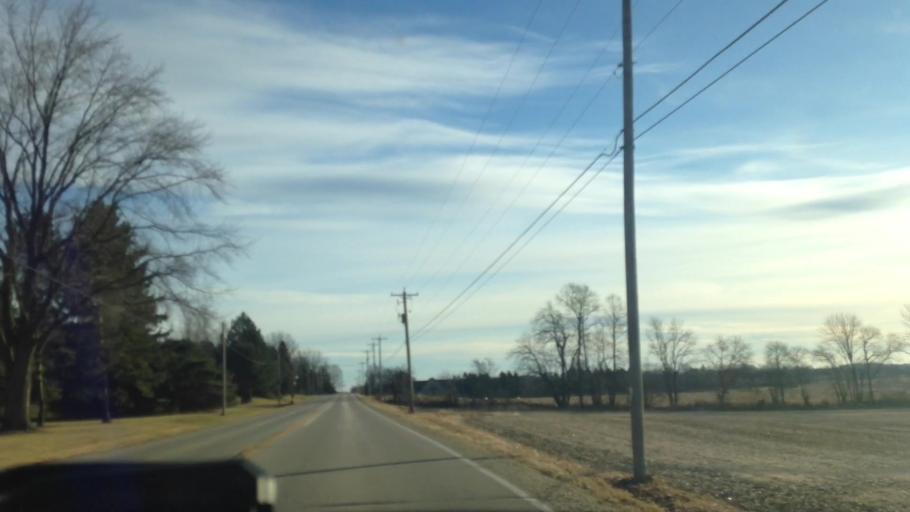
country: US
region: Wisconsin
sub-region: Washington County
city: Jackson
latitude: 43.2945
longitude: -88.1296
